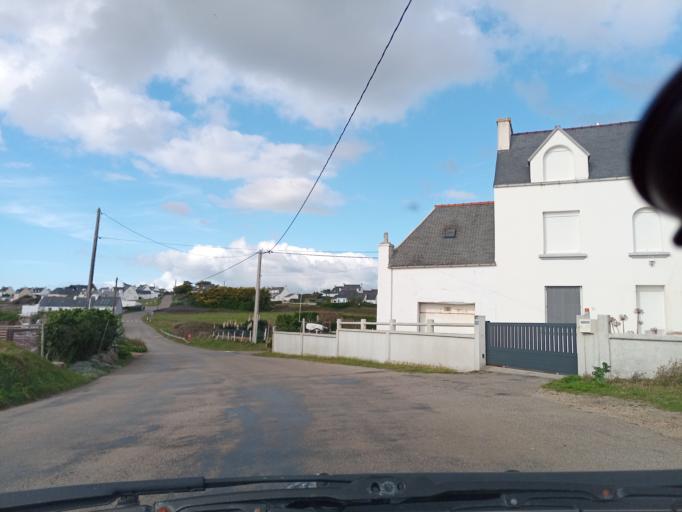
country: FR
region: Brittany
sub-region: Departement du Finistere
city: Plozevet
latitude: 47.9793
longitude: -4.4487
